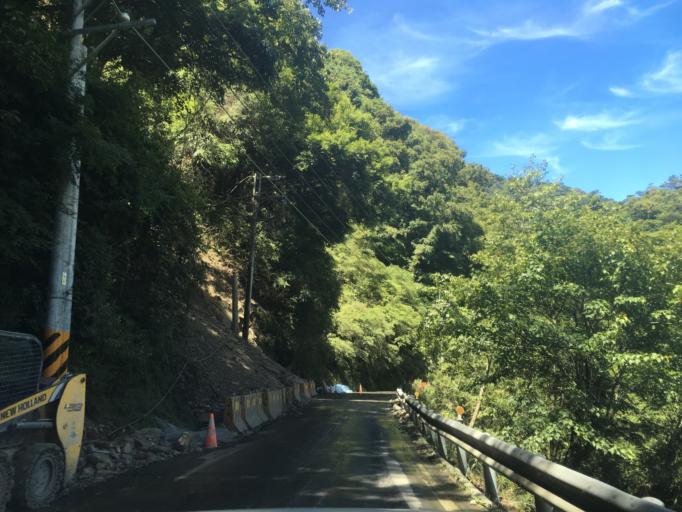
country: TW
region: Taiwan
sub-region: Nantou
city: Puli
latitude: 24.2126
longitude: 121.2672
